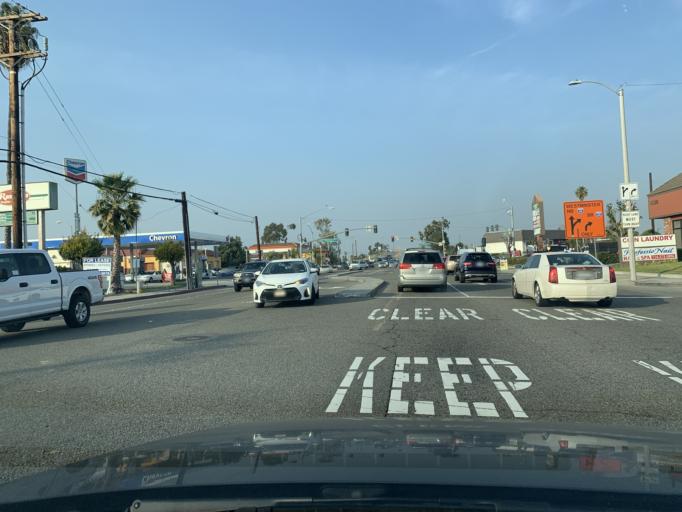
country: US
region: California
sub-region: Orange County
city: Westminster
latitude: 33.7581
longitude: -118.0246
